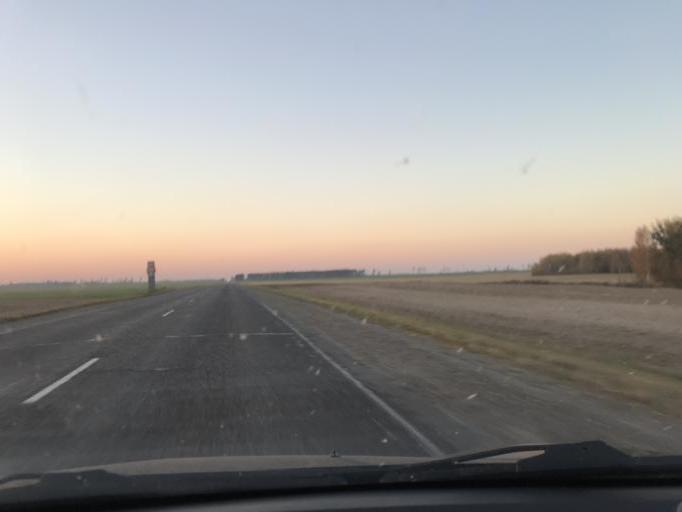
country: BY
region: Gomel
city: Horad Rechytsa
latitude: 52.1824
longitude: 30.5609
